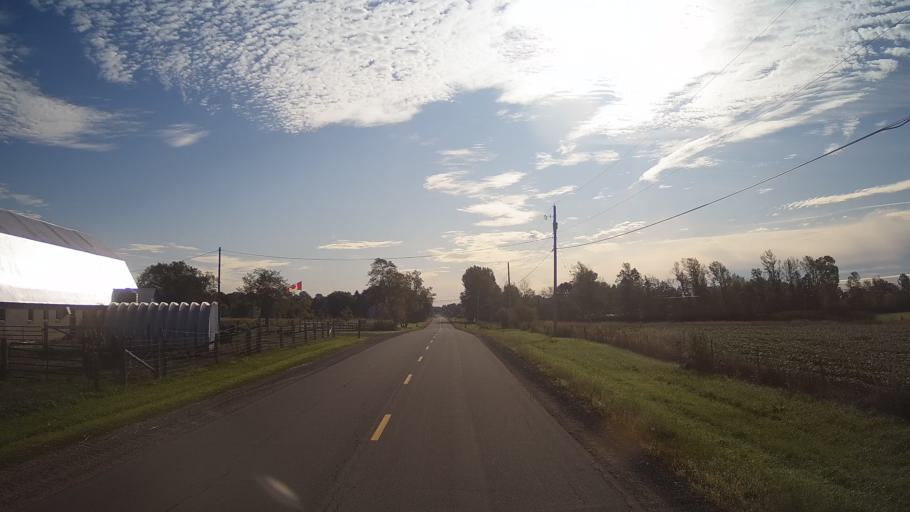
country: CA
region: Ontario
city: Gananoque
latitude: 44.4013
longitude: -76.0742
